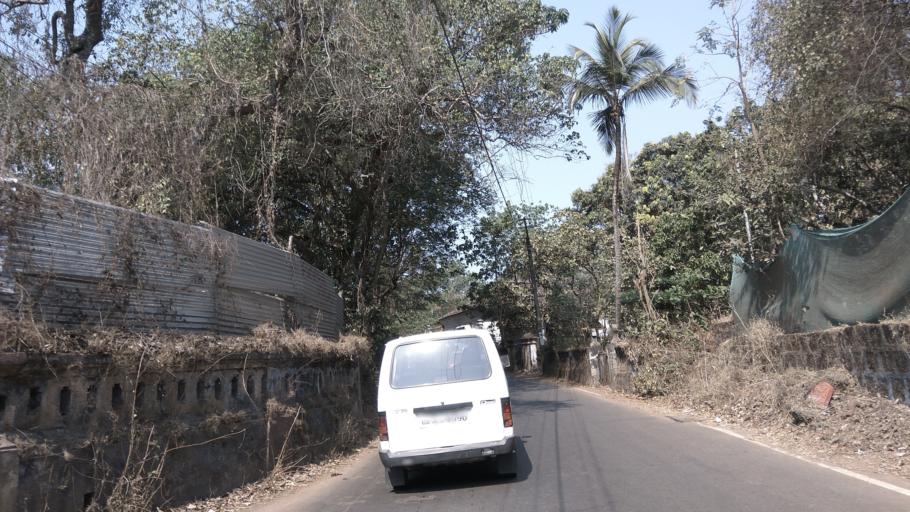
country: IN
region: Goa
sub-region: North Goa
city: Vagator
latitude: 15.5945
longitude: 73.7536
